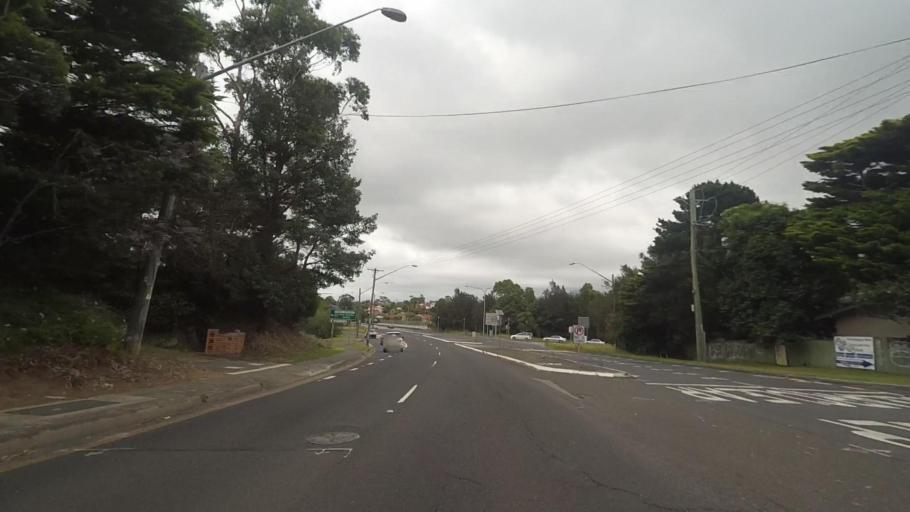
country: AU
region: New South Wales
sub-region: Wollongong
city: West Wollongong
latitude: -34.4279
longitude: 150.8686
